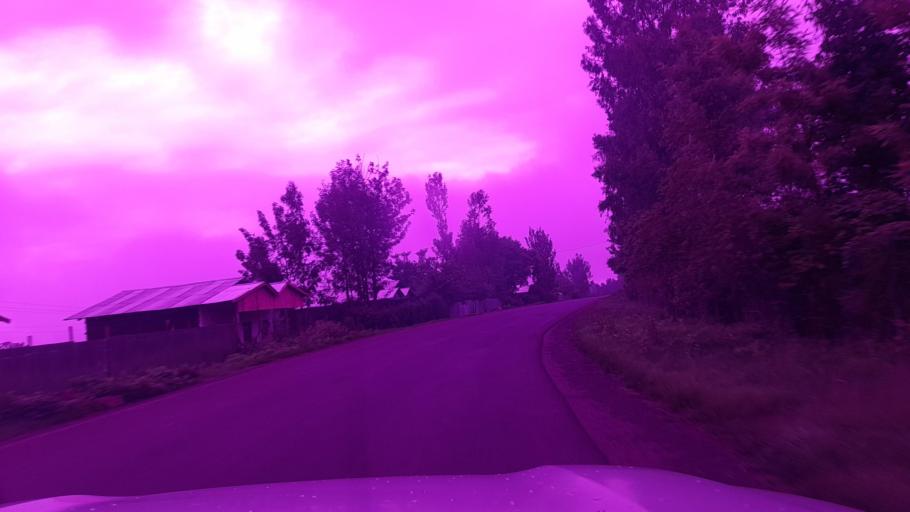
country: ET
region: Oromiya
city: Waliso
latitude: 8.1752
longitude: 37.5632
